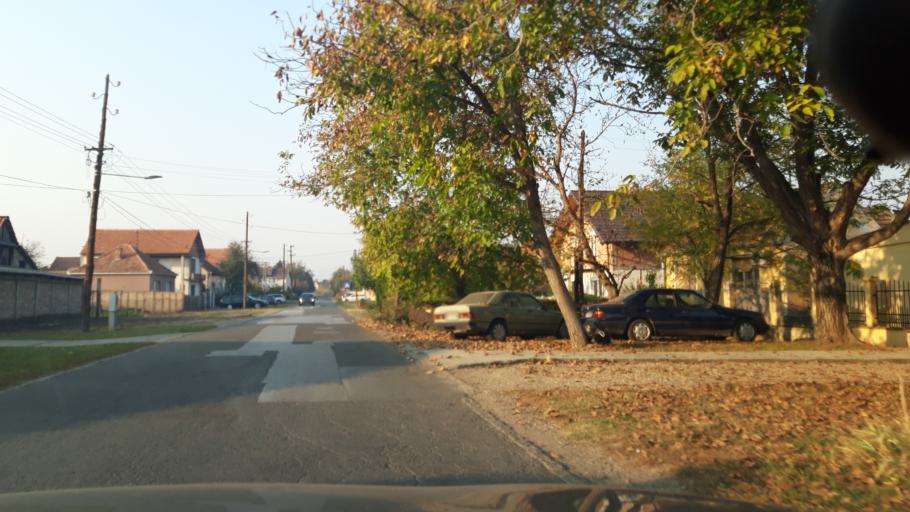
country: RS
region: Autonomna Pokrajina Vojvodina
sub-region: Sremski Okrug
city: Stara Pazova
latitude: 44.9952
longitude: 20.1455
